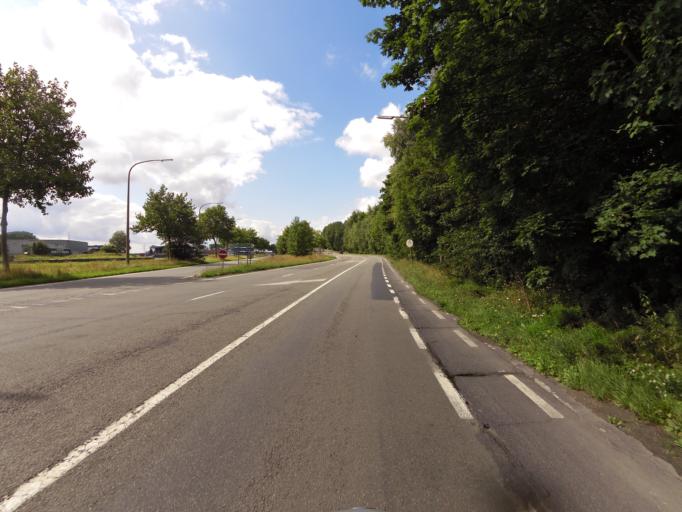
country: BE
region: Wallonia
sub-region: Province du Hainaut
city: Quaregnon
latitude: 50.4787
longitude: 3.8853
